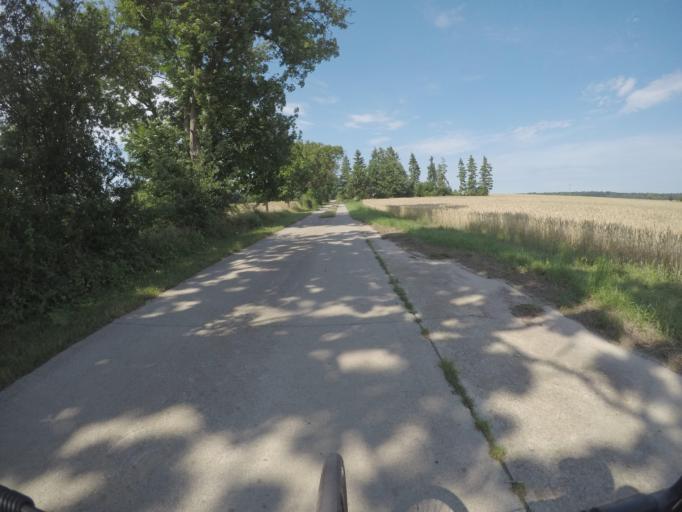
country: DE
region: Mecklenburg-Vorpommern
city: Gingst
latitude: 54.4177
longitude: 13.2559
